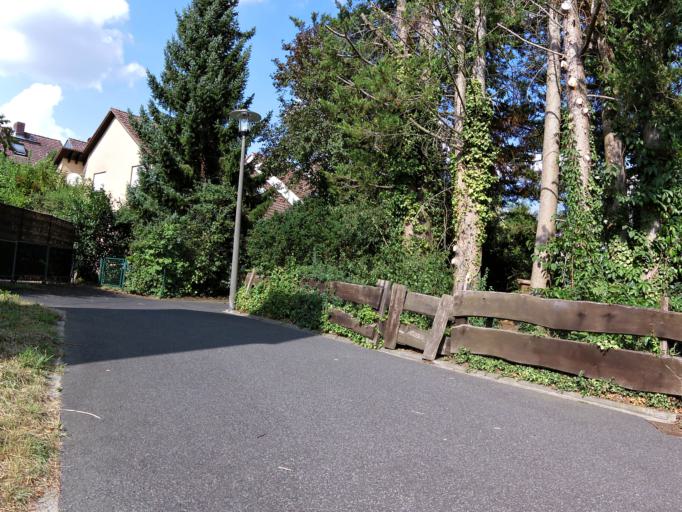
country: DE
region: Bavaria
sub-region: Regierungsbezirk Unterfranken
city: Estenfeld
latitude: 49.8239
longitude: 10.0001
